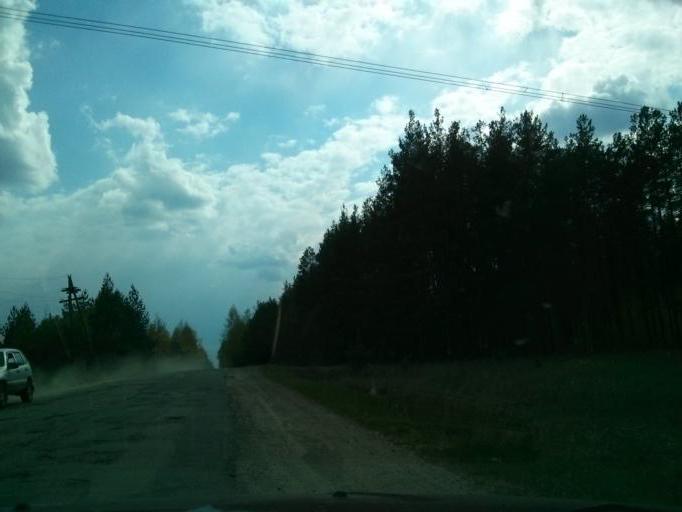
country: RU
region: Nizjnij Novgorod
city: Shimorskoye
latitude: 55.4519
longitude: 41.9812
